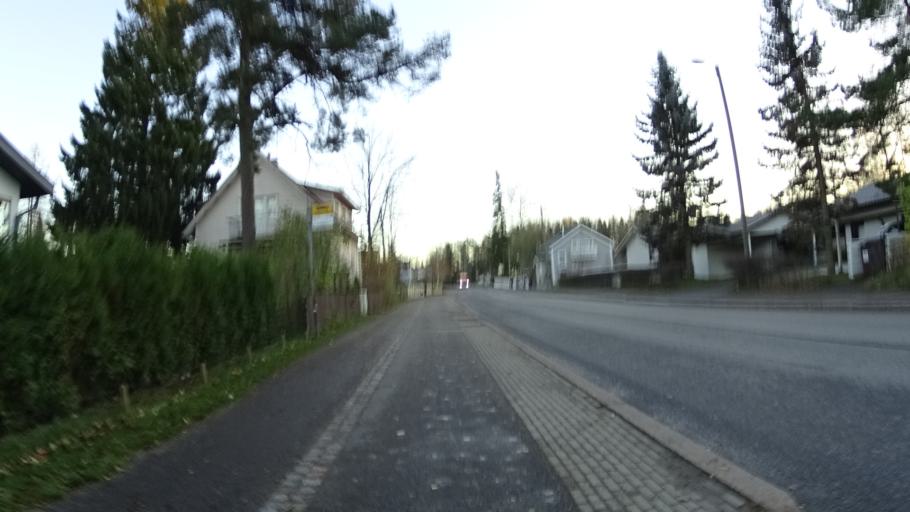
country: FI
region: Uusimaa
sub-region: Helsinki
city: Helsinki
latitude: 60.2467
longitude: 24.9433
